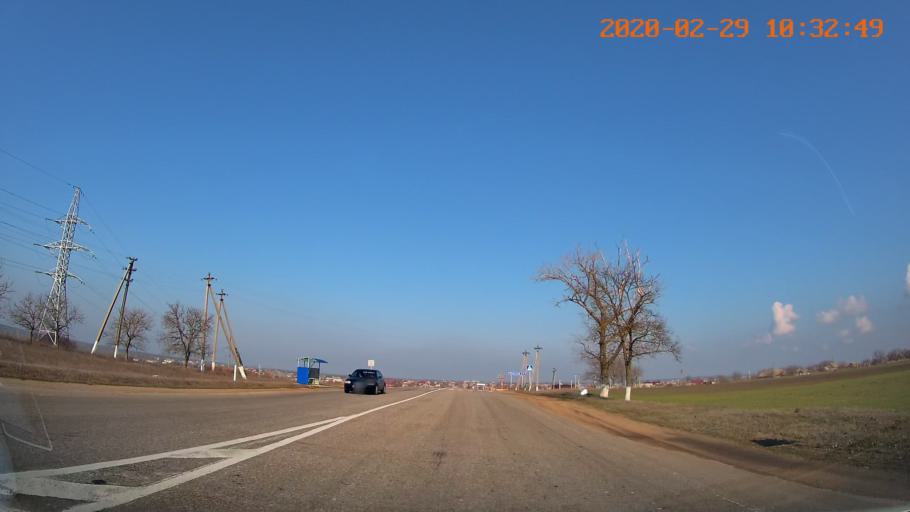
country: UA
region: Odessa
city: Velykoploske
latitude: 46.9654
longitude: 29.5509
